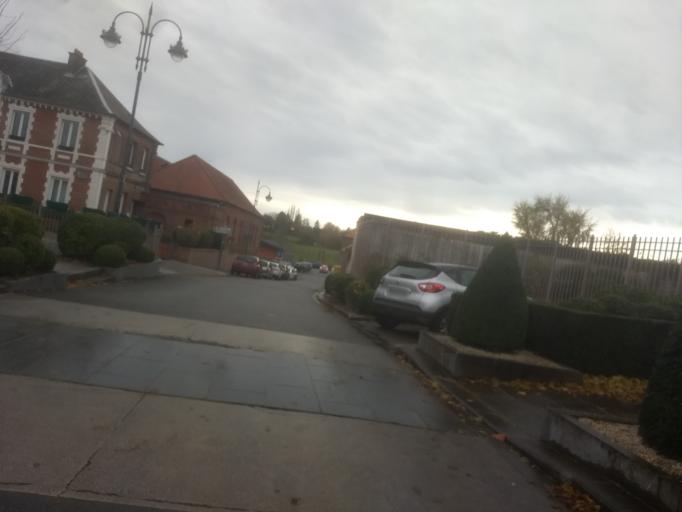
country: FR
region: Nord-Pas-de-Calais
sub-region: Departement du Pas-de-Calais
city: Dainville
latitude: 50.2810
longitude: 2.7222
